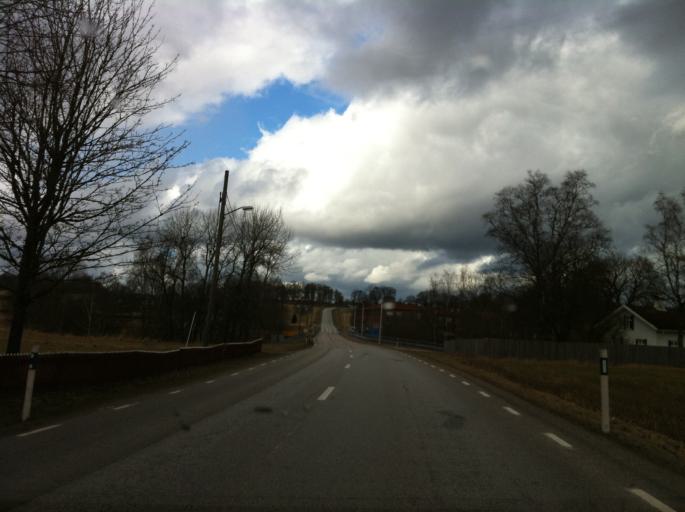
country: SE
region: Vaestra Goetaland
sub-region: Ulricehamns Kommun
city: Ulricehamn
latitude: 57.6513
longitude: 13.4375
